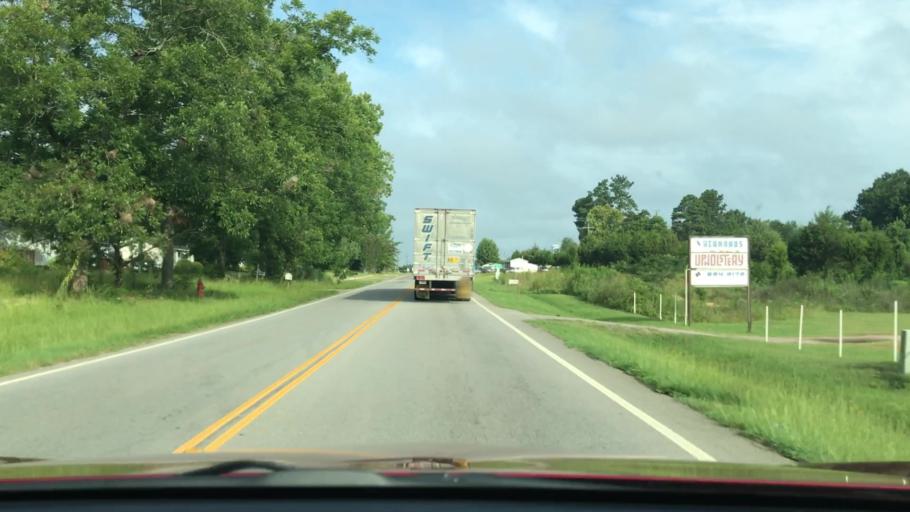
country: US
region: South Carolina
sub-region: Barnwell County
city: Williston
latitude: 33.6475
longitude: -81.3529
